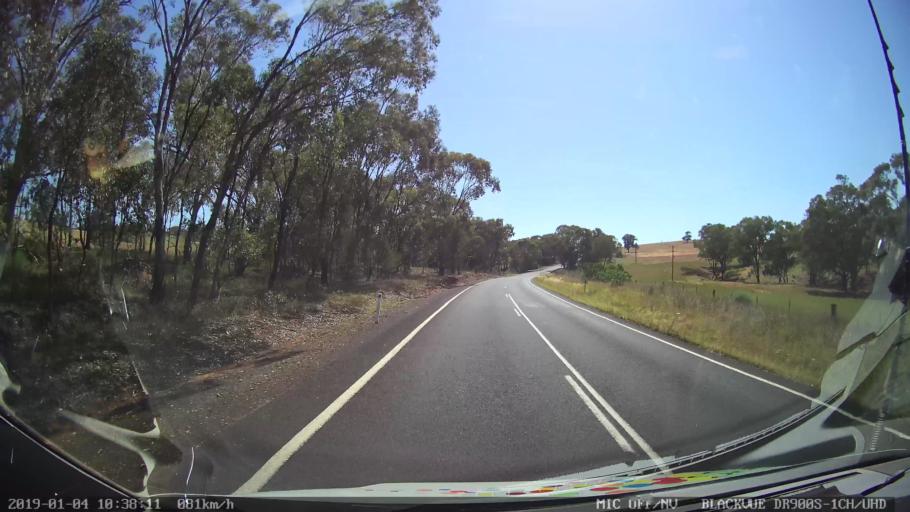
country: AU
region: New South Wales
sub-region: Cabonne
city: Molong
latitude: -33.2937
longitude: 148.7053
